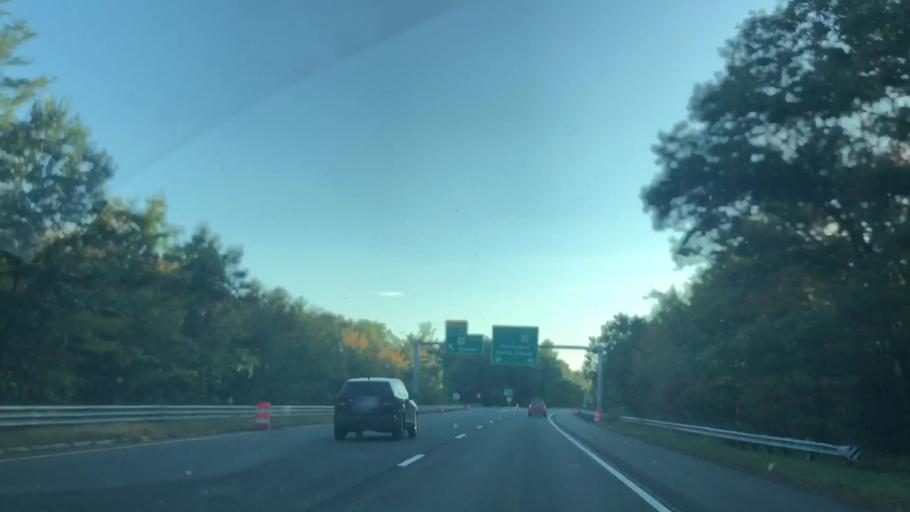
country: US
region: Massachusetts
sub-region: Franklin County
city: Greenfield
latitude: 42.6209
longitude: -72.5904
